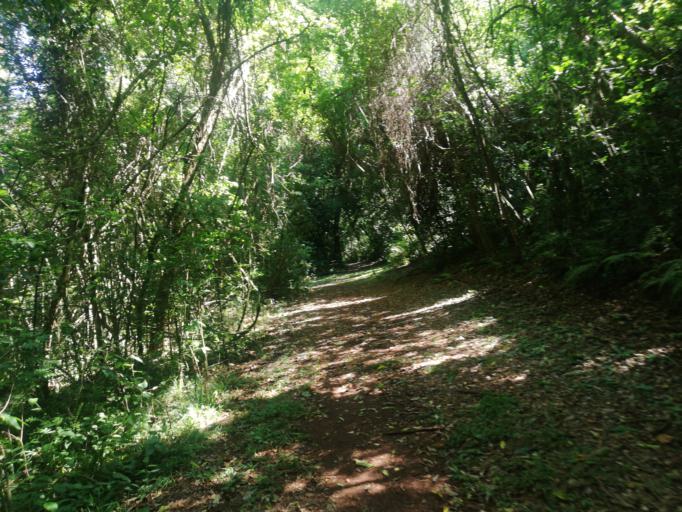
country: AR
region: Misiones
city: Cerro Azul
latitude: -27.7478
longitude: -55.5609
